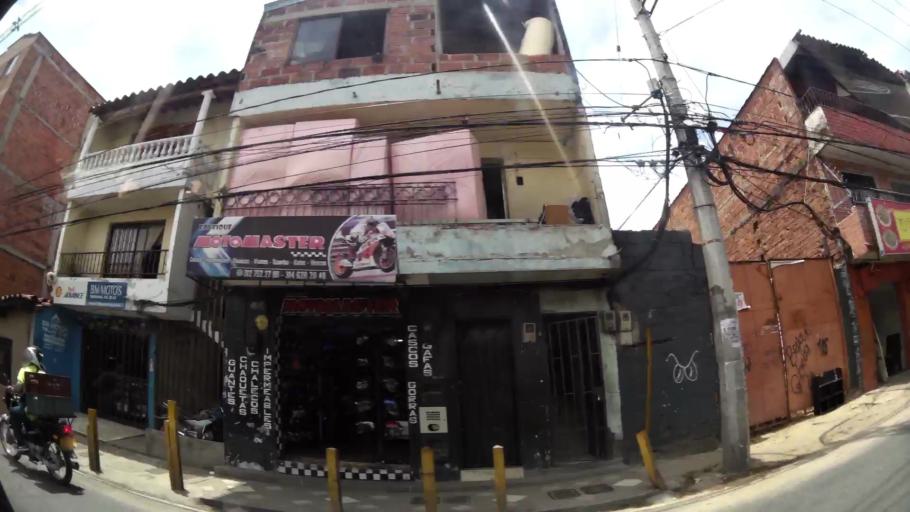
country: CO
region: Antioquia
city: Bello
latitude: 6.3310
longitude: -75.5581
